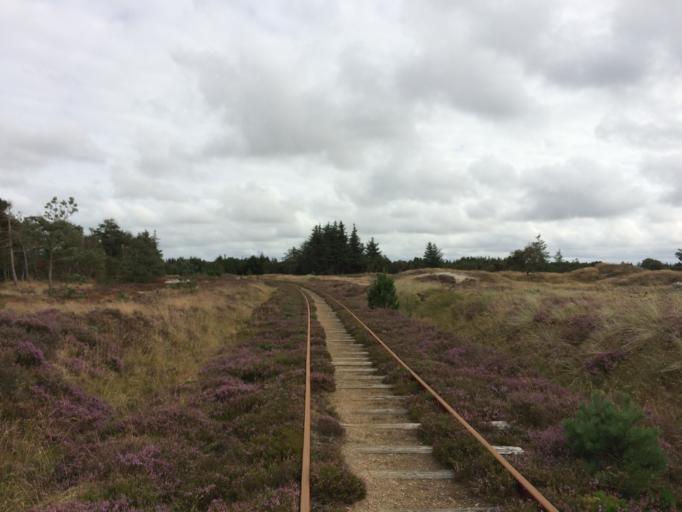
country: DK
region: South Denmark
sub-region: Varde Kommune
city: Oksbol
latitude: 55.7894
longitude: 8.2328
